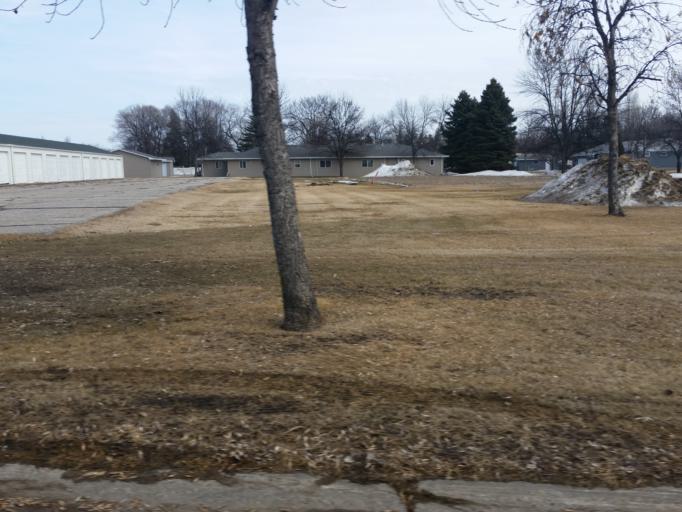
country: US
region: North Dakota
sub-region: Walsh County
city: Grafton
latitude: 48.4113
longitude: -97.4234
